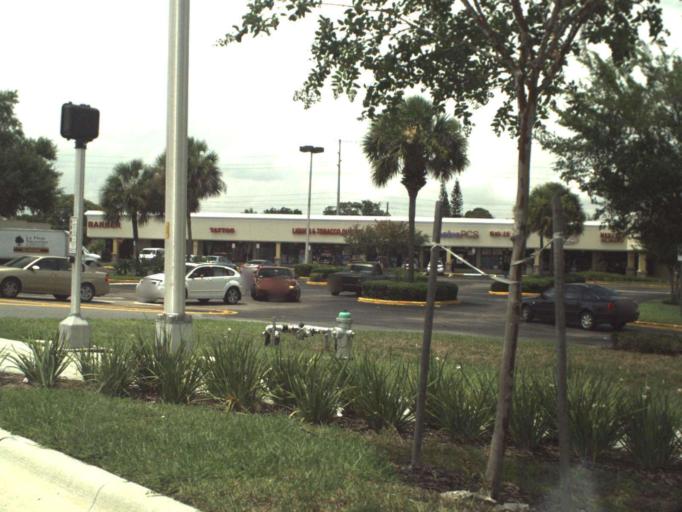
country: US
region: Florida
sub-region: Seminole County
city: Fern Park
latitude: 28.6488
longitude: -81.3247
